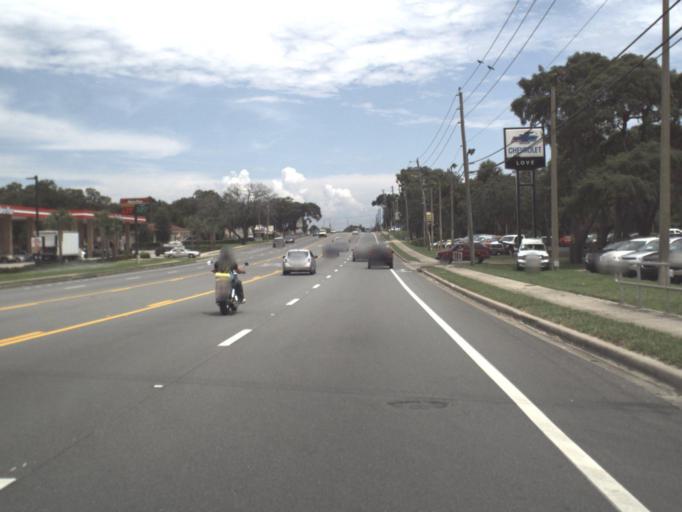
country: US
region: Florida
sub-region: Citrus County
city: Inverness
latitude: 28.8397
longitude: -82.3591
